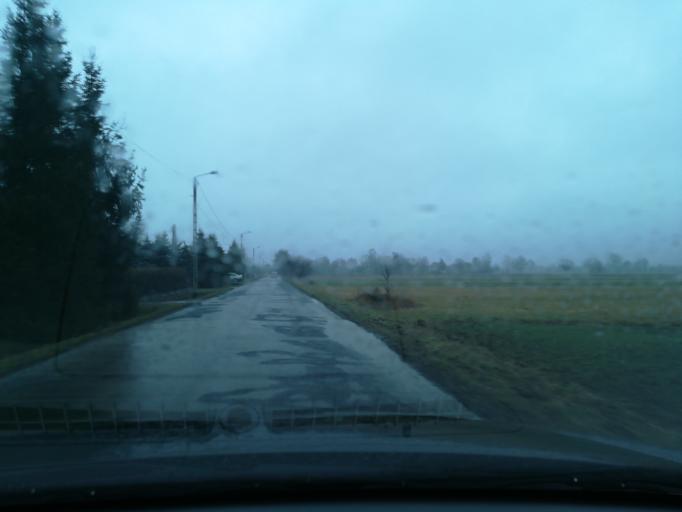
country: PL
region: Subcarpathian Voivodeship
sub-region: Powiat lancucki
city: Kosina
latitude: 50.0938
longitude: 22.3458
